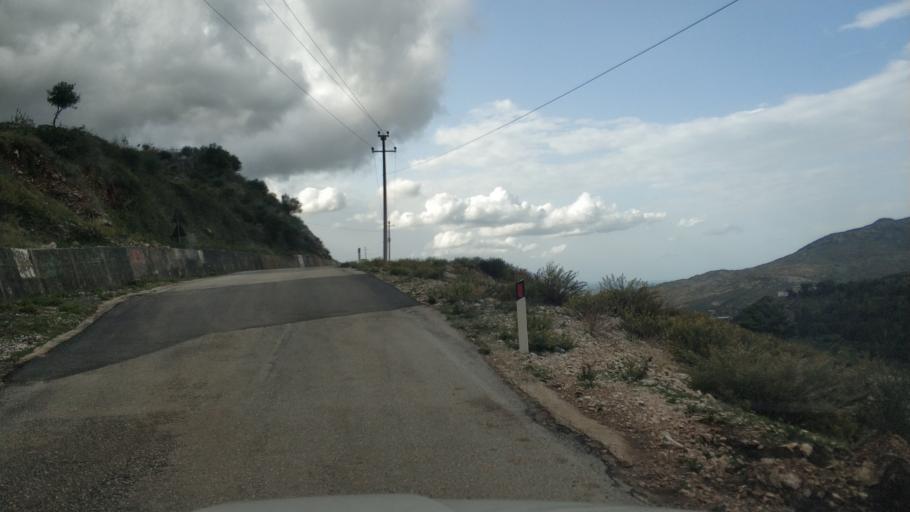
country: AL
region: Vlore
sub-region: Rrethi i Vlores
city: Orikum
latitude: 40.2622
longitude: 19.5227
